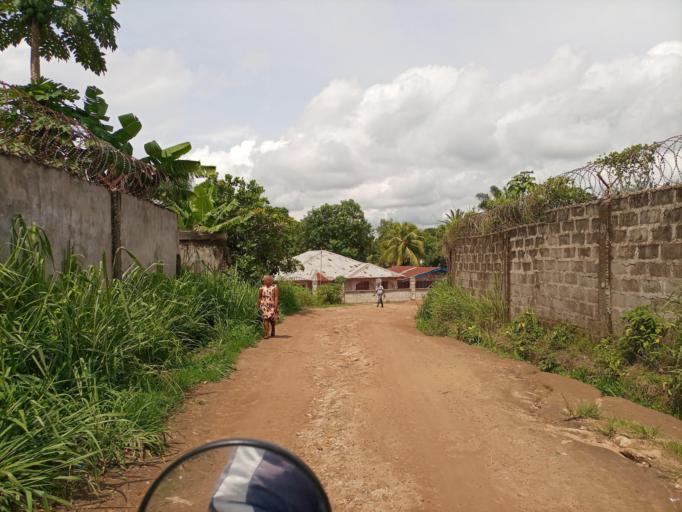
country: SL
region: Southern Province
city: Bo
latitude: 7.9713
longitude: -11.7629
